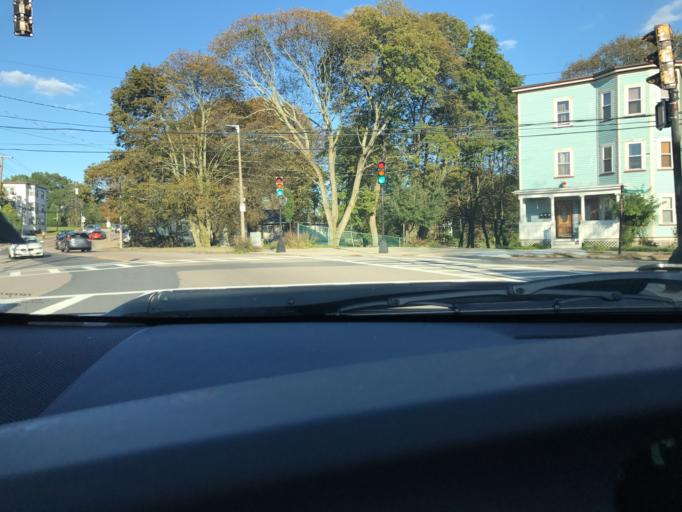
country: US
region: Massachusetts
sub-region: Suffolk County
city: Jamaica Plain
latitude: 42.2780
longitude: -71.1220
